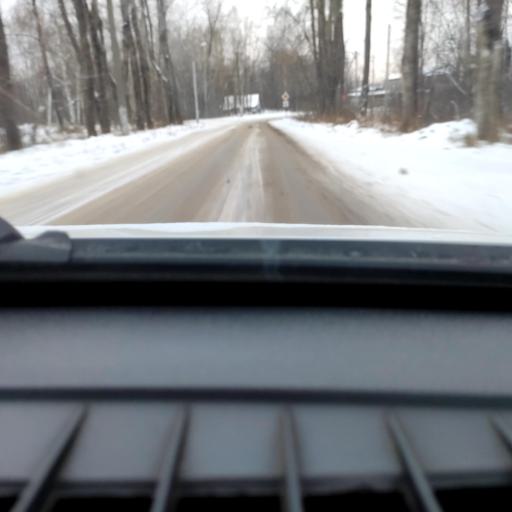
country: RU
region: Perm
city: Perm
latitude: 58.0979
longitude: 56.3679
